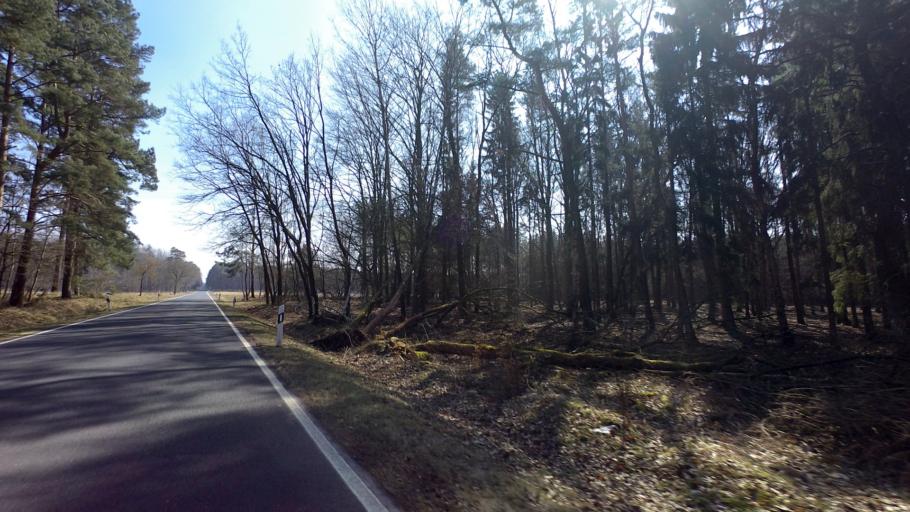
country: DE
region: Saxony-Anhalt
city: Nudersdorf
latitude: 52.0203
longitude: 12.5526
